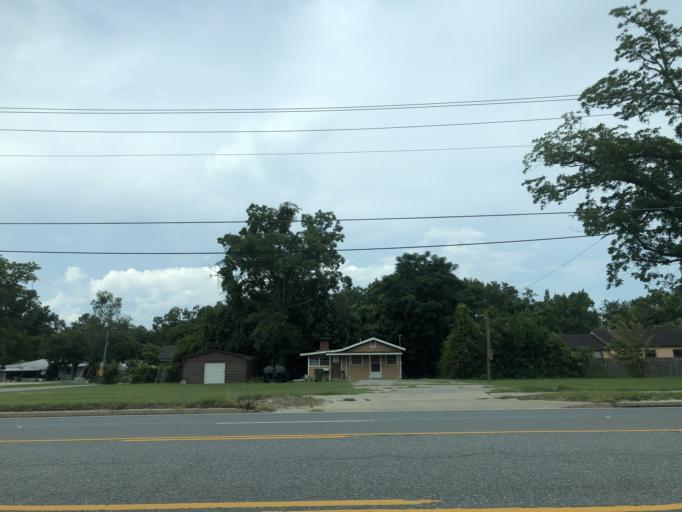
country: US
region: Georgia
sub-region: Wayne County
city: Jesup
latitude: 31.6045
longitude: -81.8775
